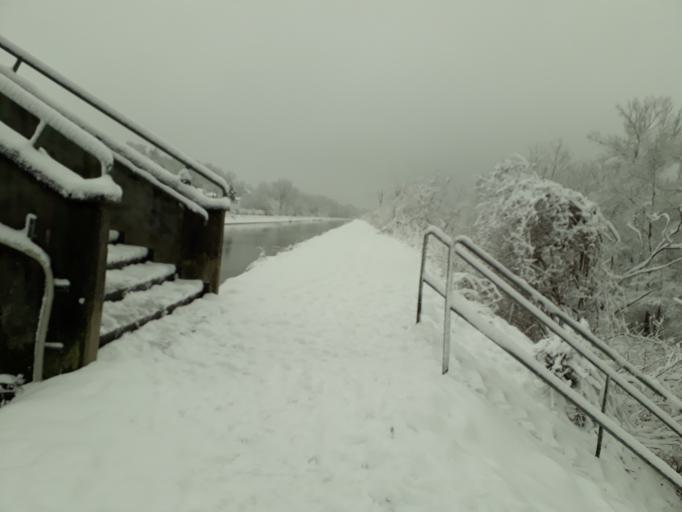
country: DE
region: Bavaria
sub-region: Upper Bavaria
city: Unterfoehring
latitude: 48.1933
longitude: 11.6371
